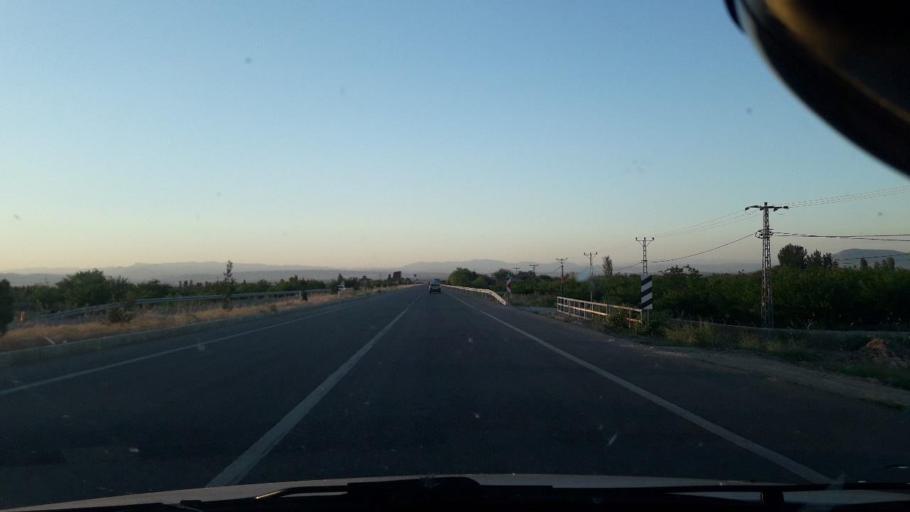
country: TR
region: Malatya
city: Malatya
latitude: 38.4365
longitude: 38.2250
